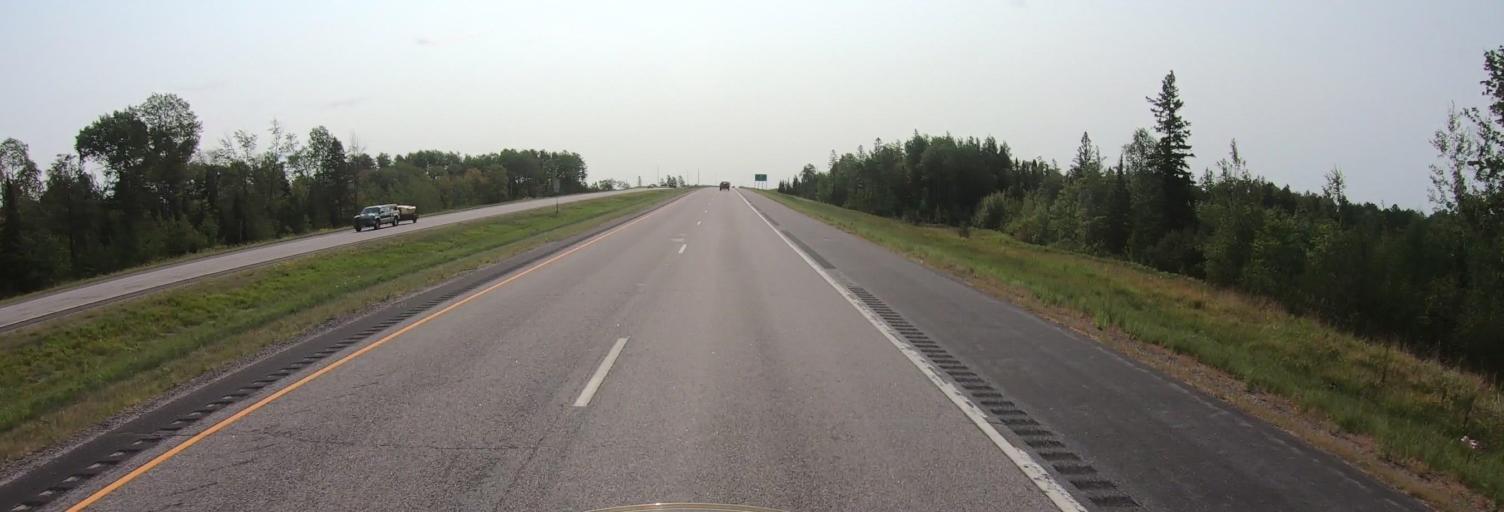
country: US
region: Minnesota
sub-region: Saint Louis County
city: Parkville
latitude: 47.5923
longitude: -92.5506
